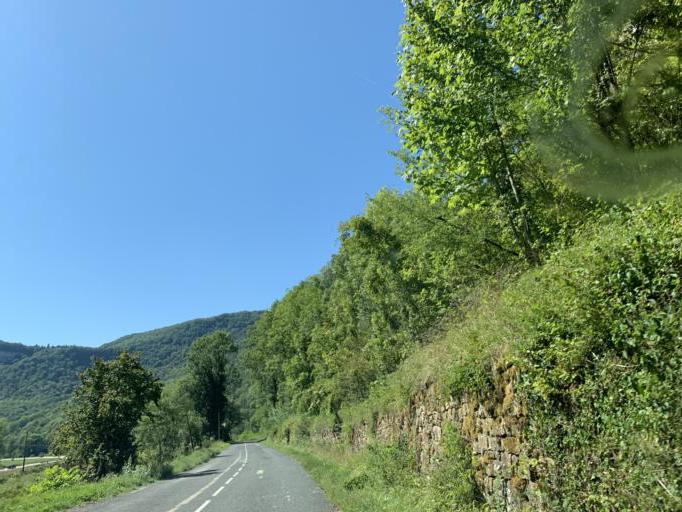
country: FR
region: Rhone-Alpes
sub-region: Departement de l'Ain
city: Saint-Rambert-en-Bugey
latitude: 45.9362
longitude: 5.4184
